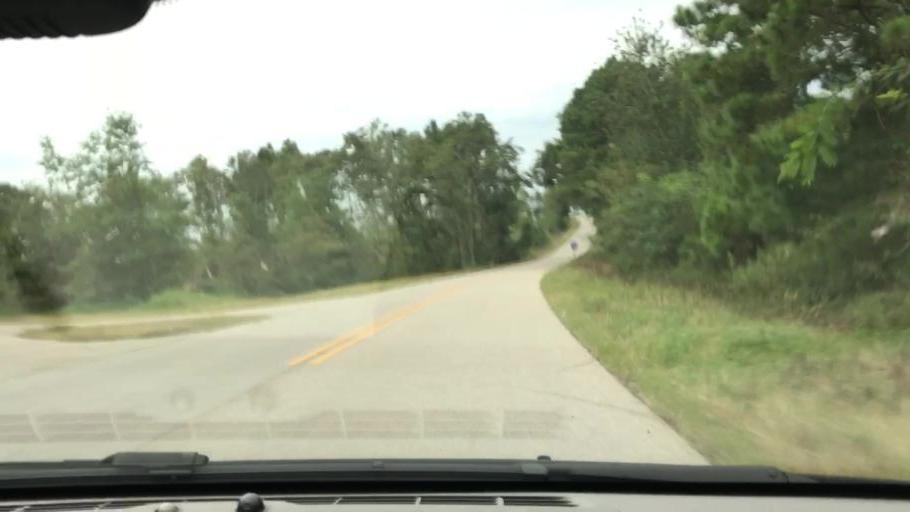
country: US
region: Alabama
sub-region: Houston County
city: Ashford
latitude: 31.2469
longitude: -85.1697
